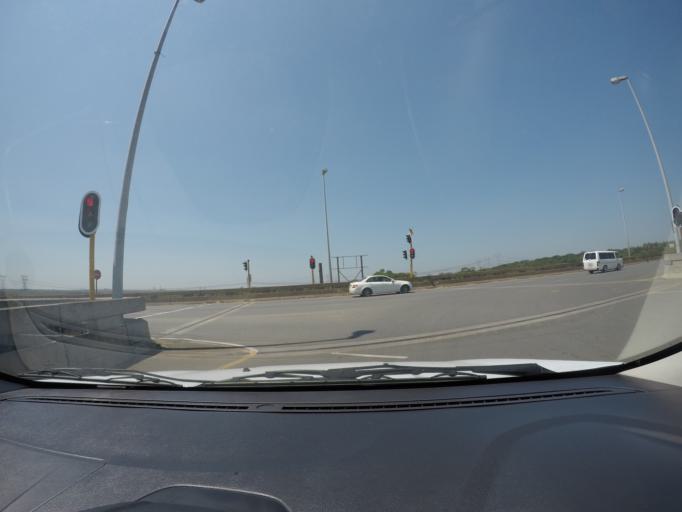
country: ZA
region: KwaZulu-Natal
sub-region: uThungulu District Municipality
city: Empangeni
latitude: -28.7752
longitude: 31.9587
